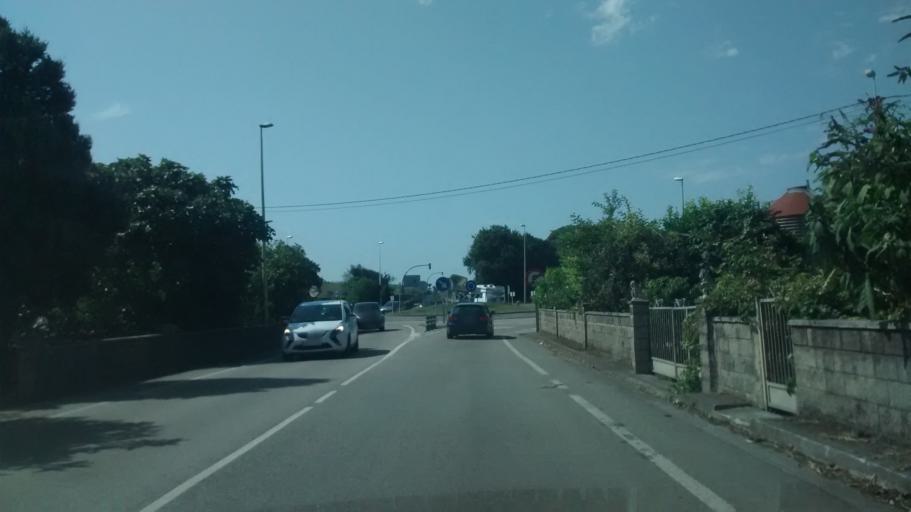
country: ES
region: Cantabria
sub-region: Provincia de Cantabria
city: Arnuero
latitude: 43.4555
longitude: -3.5540
